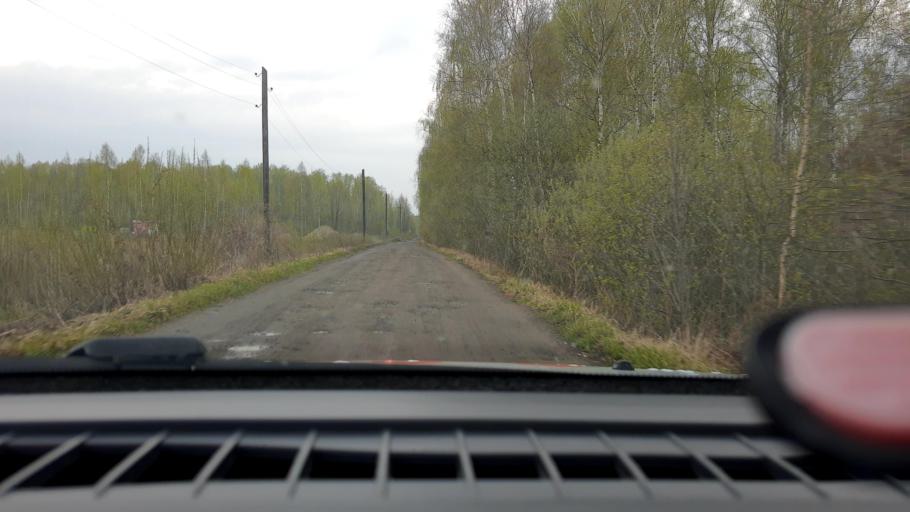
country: RU
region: Nizjnij Novgorod
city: Gorbatovka
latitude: 56.3037
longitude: 43.7696
